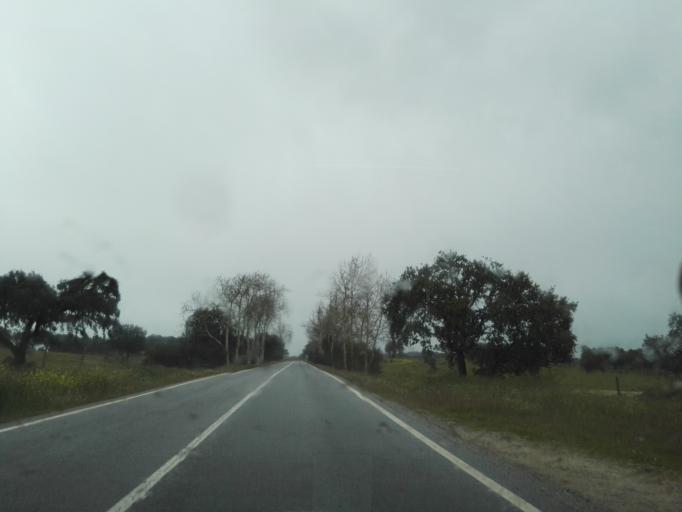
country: PT
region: Portalegre
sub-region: Arronches
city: Arronches
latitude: 39.0607
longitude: -7.2732
